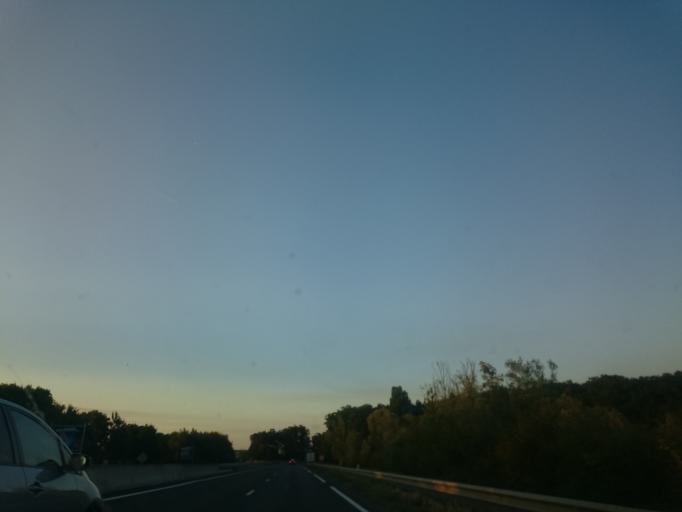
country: FR
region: Ile-de-France
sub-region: Departement de l'Essonne
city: Marolles-en-Hurepoix
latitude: 48.5845
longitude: 2.3059
